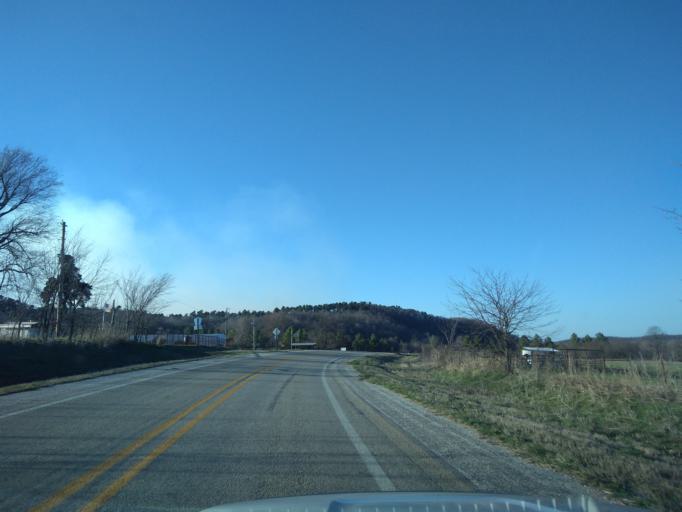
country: US
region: Arkansas
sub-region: Washington County
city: Farmington
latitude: 36.1004
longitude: -94.3490
